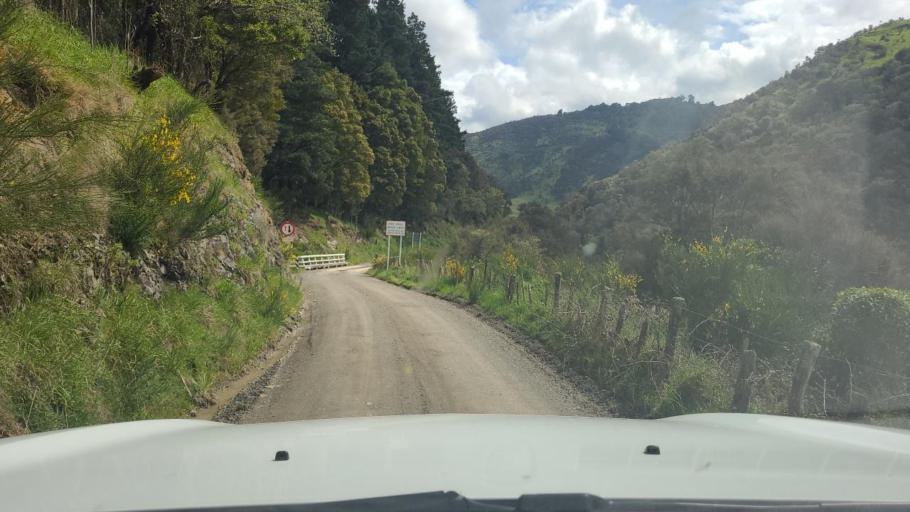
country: NZ
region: Wellington
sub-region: Masterton District
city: Masterton
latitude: -40.9322
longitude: 175.5006
